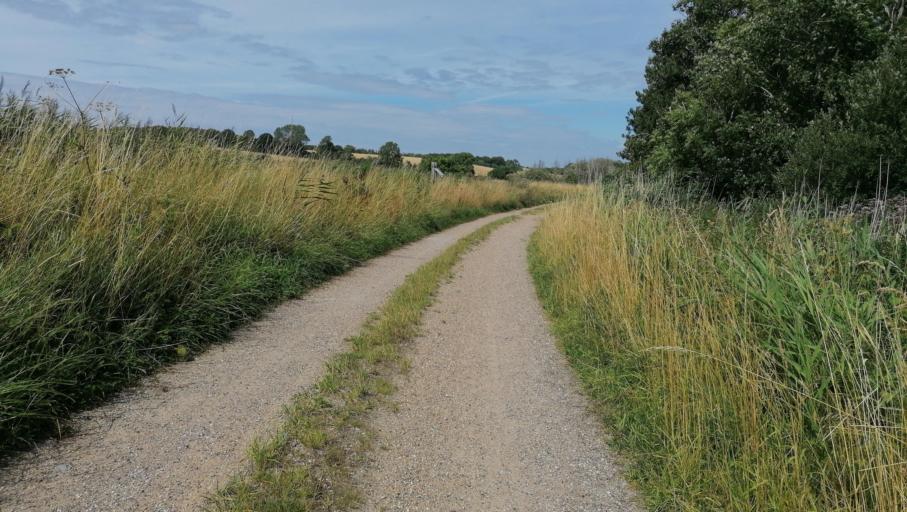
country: DK
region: Zealand
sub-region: Odsherred Kommune
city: Horve
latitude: 55.7812
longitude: 11.4190
